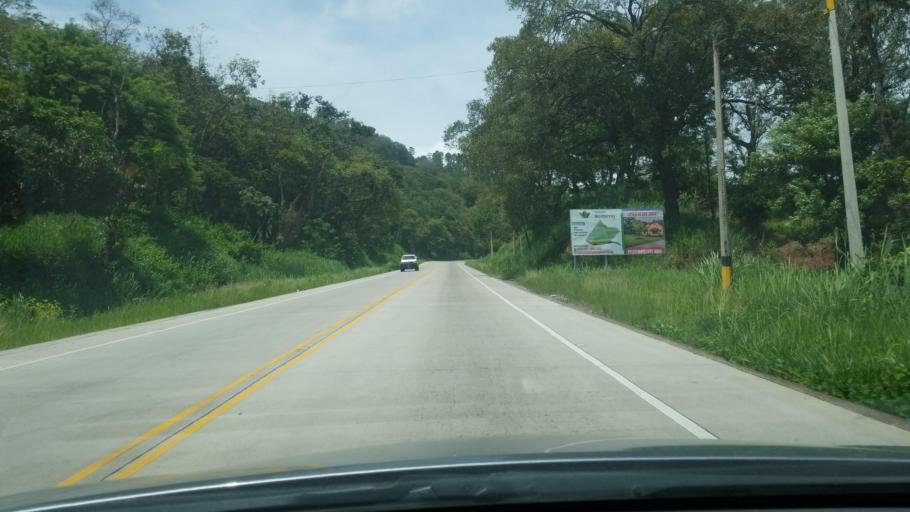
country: HN
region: Copan
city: Agua Caliente
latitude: 14.8700
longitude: -88.7848
